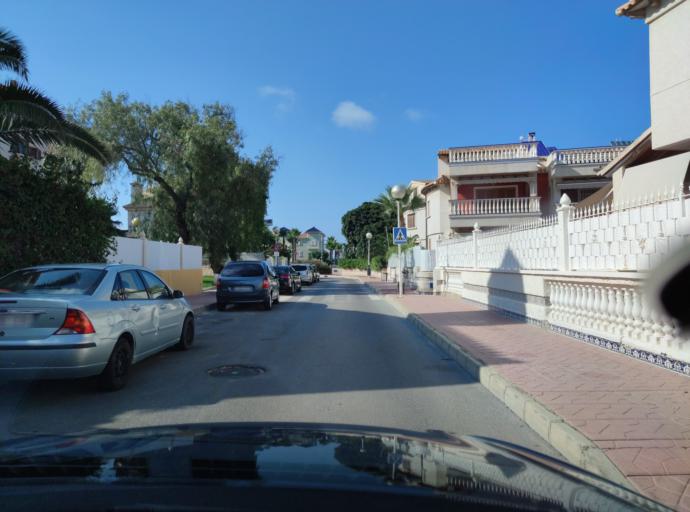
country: ES
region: Valencia
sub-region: Provincia de Alicante
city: Guardamar del Segura
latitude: 38.0645
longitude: -0.6526
